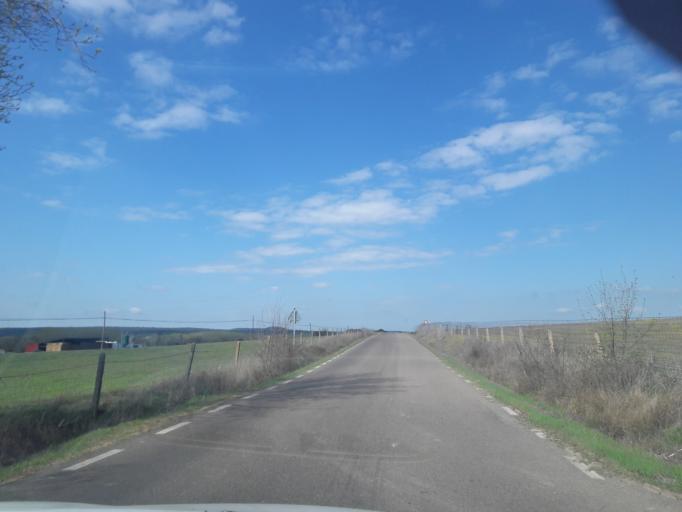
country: ES
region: Castille and Leon
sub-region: Provincia de Salamanca
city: Zamarra
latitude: 40.5673
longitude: -6.4787
